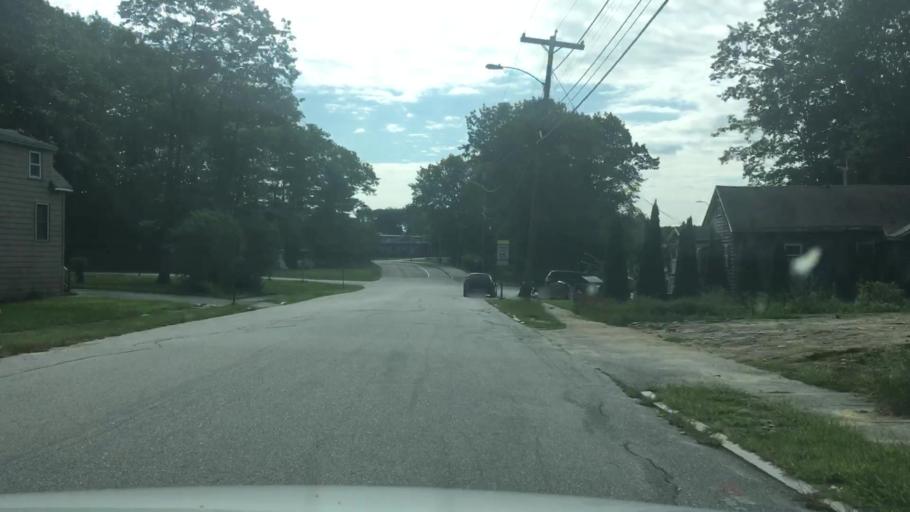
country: US
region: Maine
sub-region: Androscoggin County
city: Auburn
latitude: 44.0959
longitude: -70.2369
